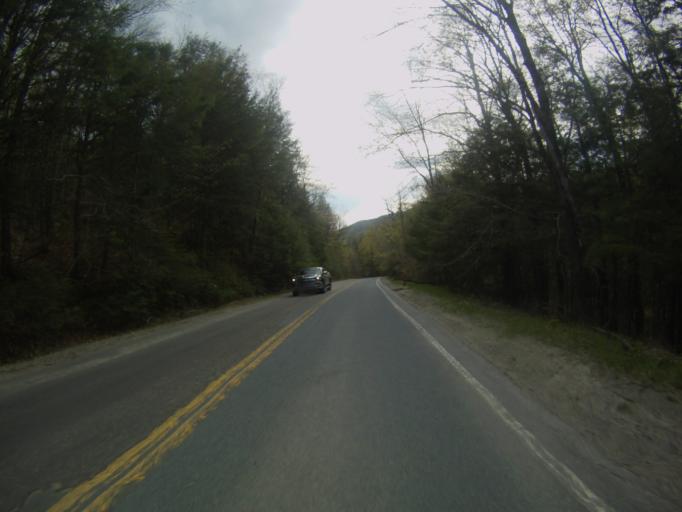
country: US
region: New York
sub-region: Warren County
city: Warrensburg
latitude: 43.8256
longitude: -73.9151
